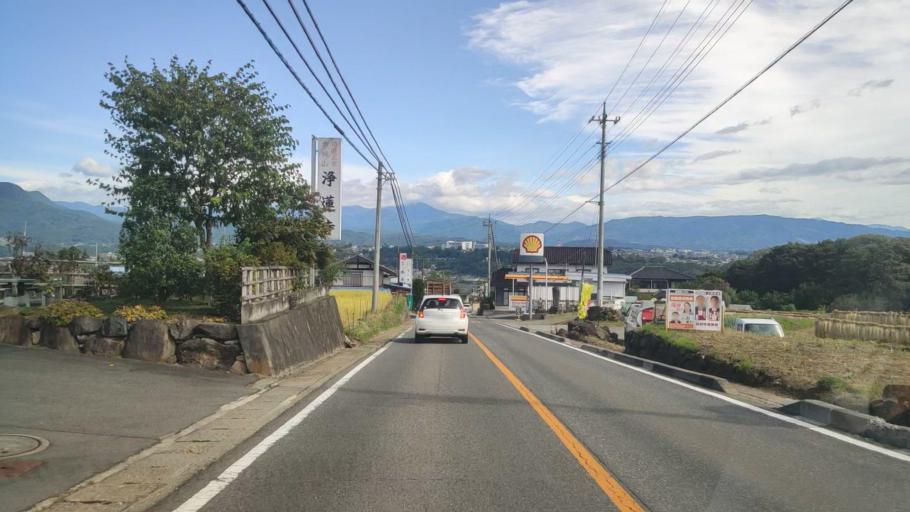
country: JP
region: Gunma
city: Numata
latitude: 36.6264
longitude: 139.0286
